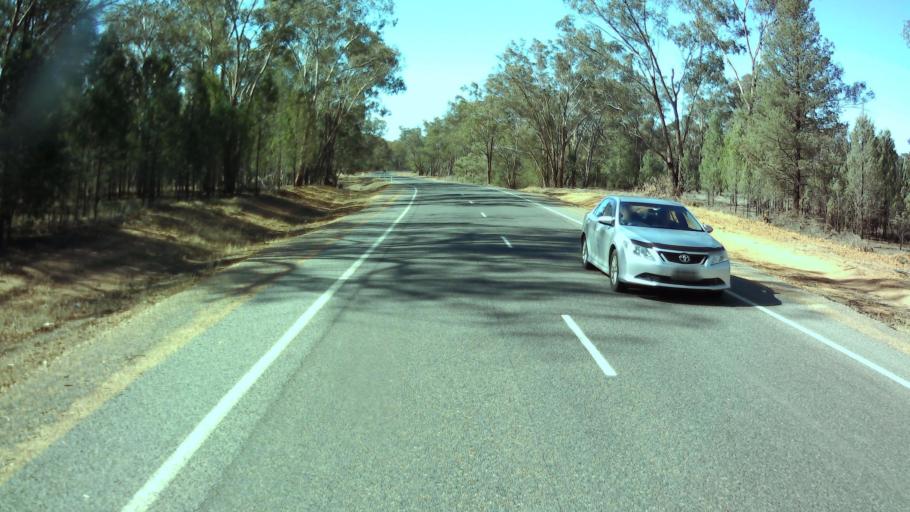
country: AU
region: New South Wales
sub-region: Weddin
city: Grenfell
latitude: -33.7591
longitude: 148.0825
